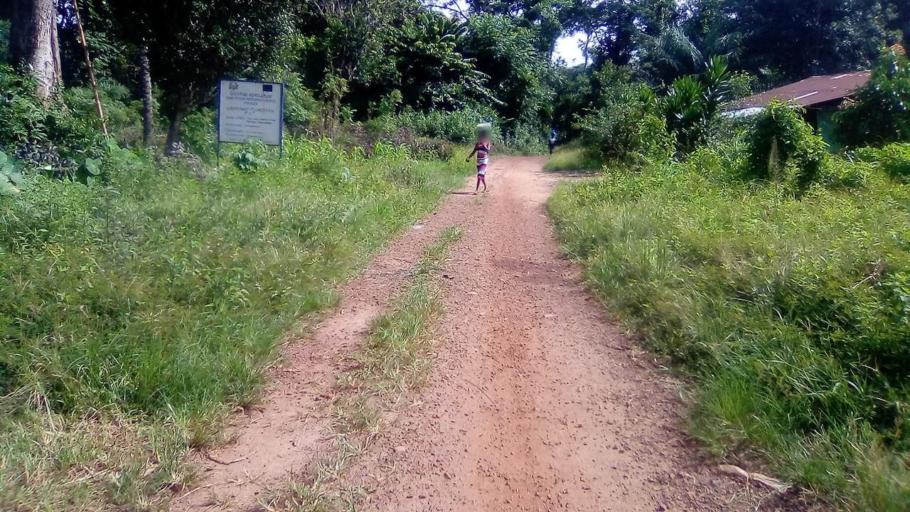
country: SL
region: Southern Province
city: Pujehun
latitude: 7.3747
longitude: -11.7285
